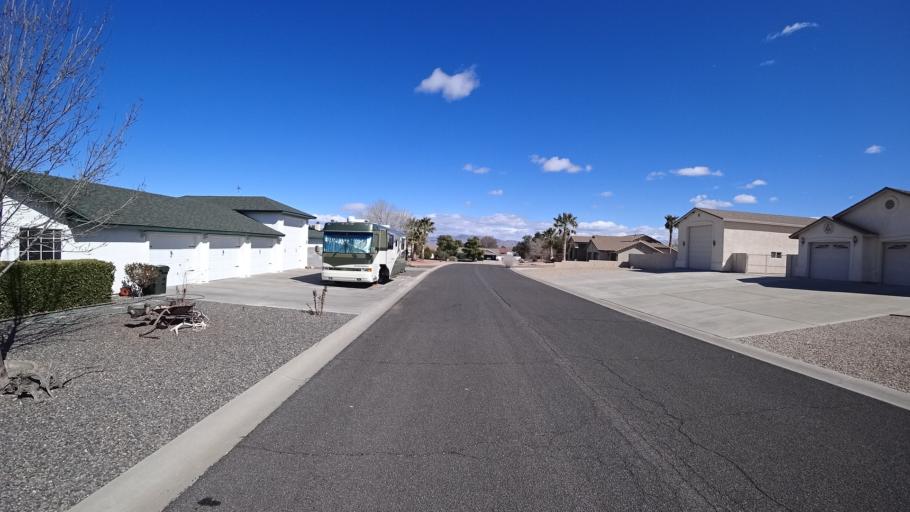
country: US
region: Arizona
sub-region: Mohave County
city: Kingman
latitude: 35.2012
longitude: -113.9656
